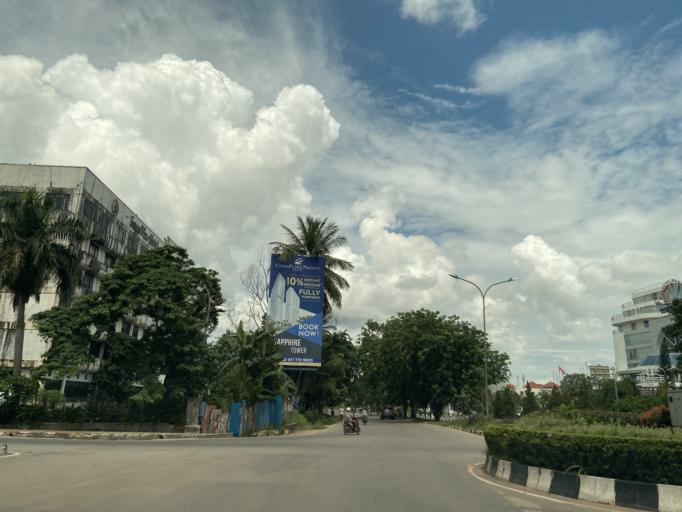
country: SG
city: Singapore
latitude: 1.1524
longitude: 104.0031
